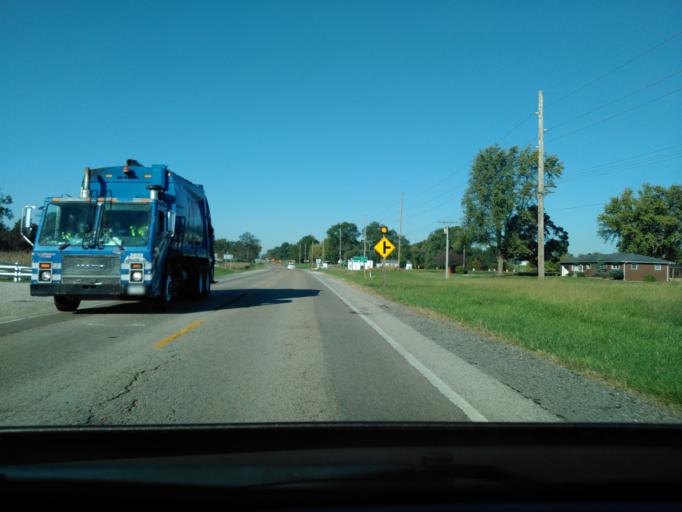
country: US
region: Illinois
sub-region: Madison County
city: Troy
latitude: 38.7174
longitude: -89.8408
